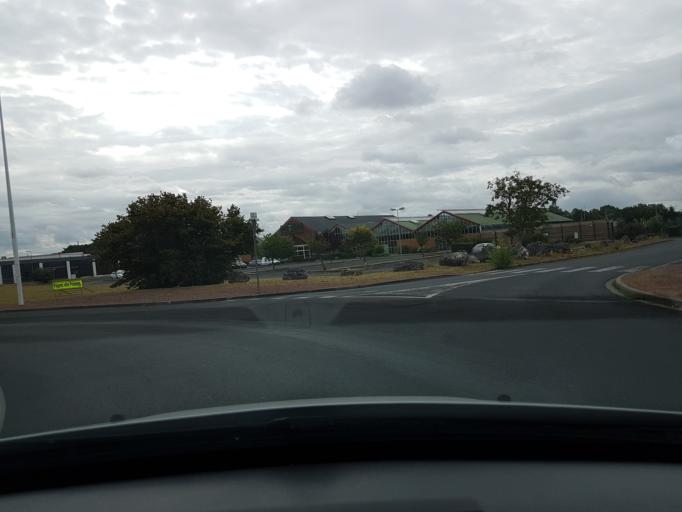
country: FR
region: Centre
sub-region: Departement d'Indre-et-Loire
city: La Ville-aux-Dames
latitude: 47.3937
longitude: 0.7846
